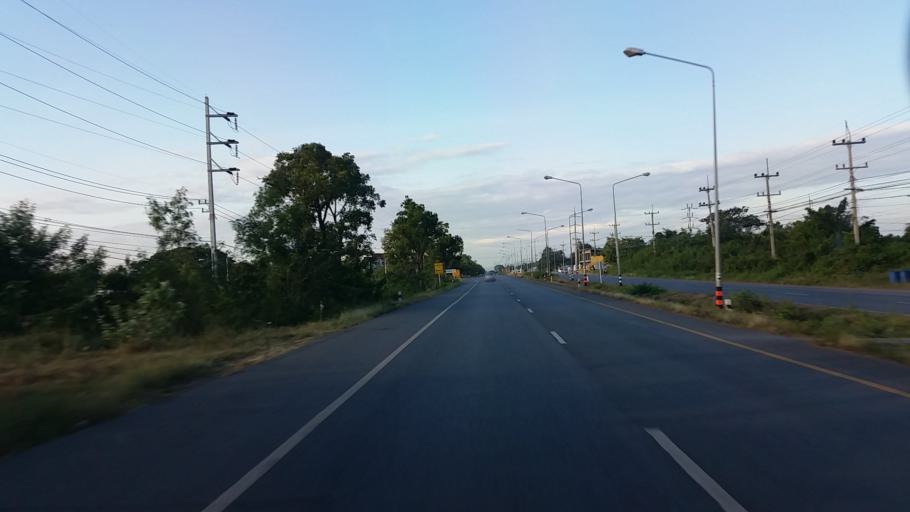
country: TH
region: Lop Buri
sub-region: Amphoe Tha Luang
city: Tha Luang
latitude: 15.0883
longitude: 101.0108
